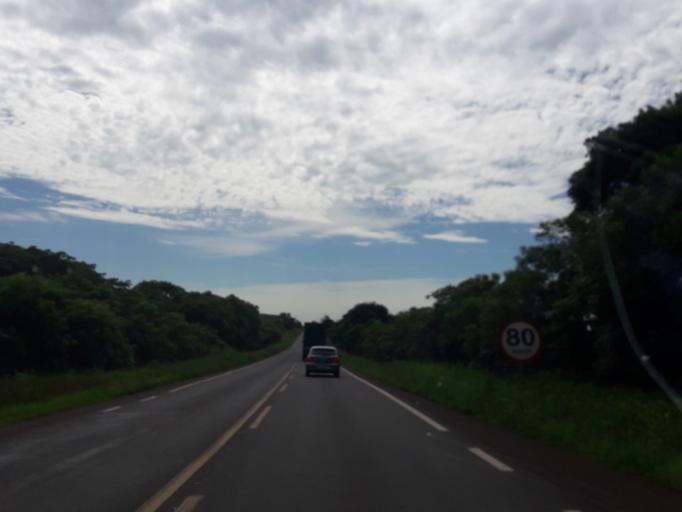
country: AR
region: Misiones
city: Bernardo de Irigoyen
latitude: -26.2782
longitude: -53.5808
